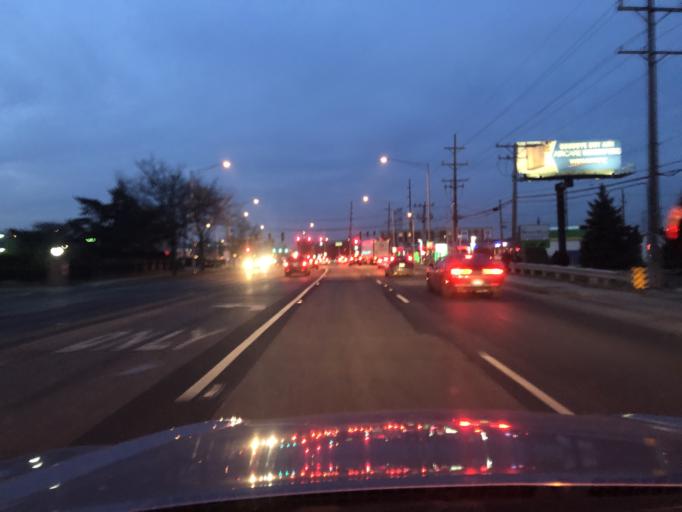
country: US
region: Illinois
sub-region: Cook County
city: Elk Grove Village
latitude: 42.0342
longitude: -87.9602
